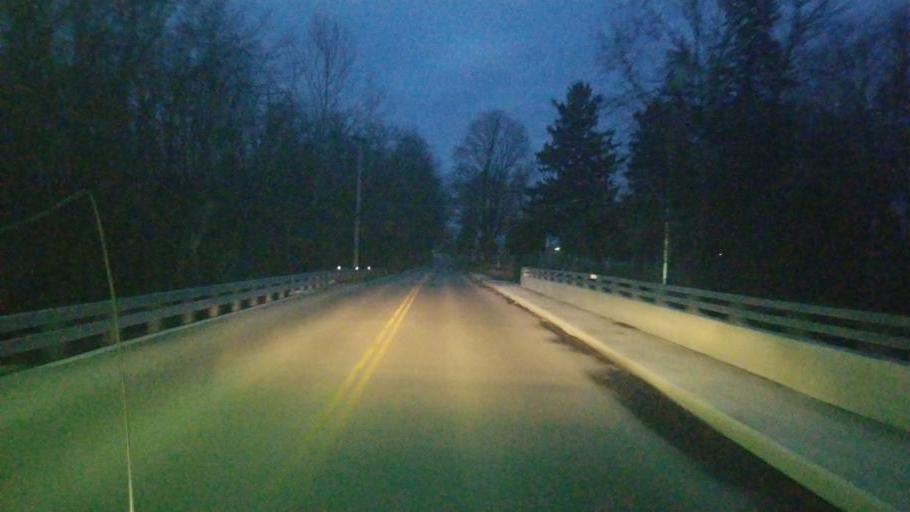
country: US
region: Ohio
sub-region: Marion County
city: Prospect
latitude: 40.4505
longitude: -83.1917
